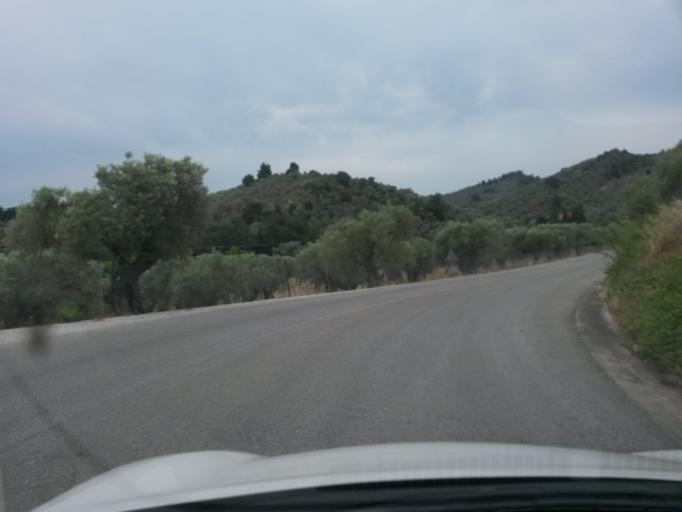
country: GR
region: North Aegean
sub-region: Nomos Lesvou
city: Skopelos
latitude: 39.0277
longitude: 26.4603
